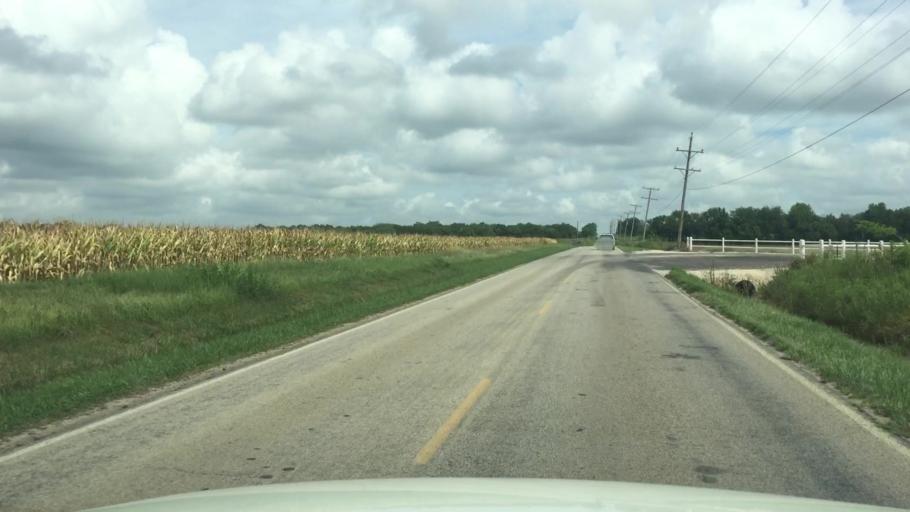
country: US
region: Kansas
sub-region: Allen County
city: Humboldt
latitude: 37.8535
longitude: -95.4369
